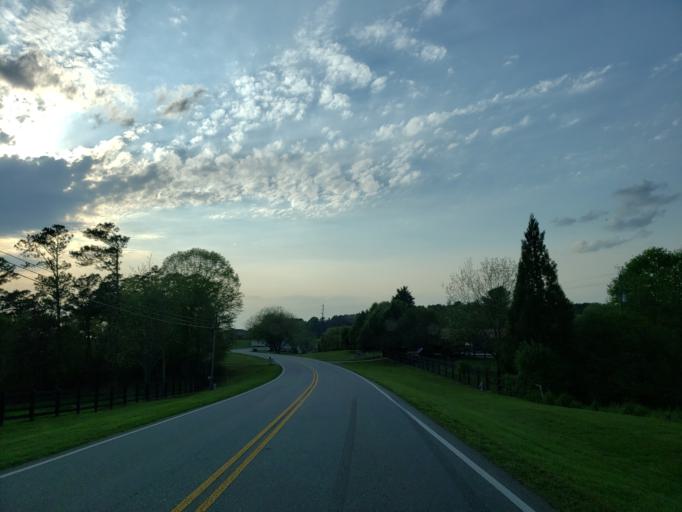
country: US
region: Georgia
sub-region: Cherokee County
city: Ball Ground
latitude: 34.2665
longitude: -84.3630
